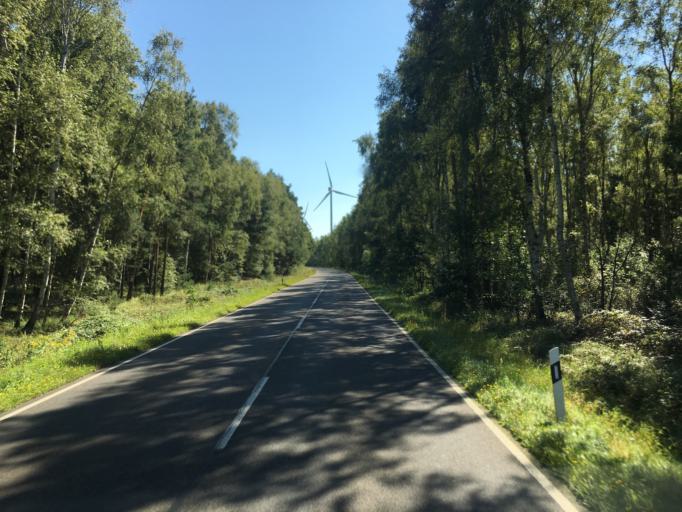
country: DE
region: Brandenburg
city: Welzow
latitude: 51.5483
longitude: 14.1574
